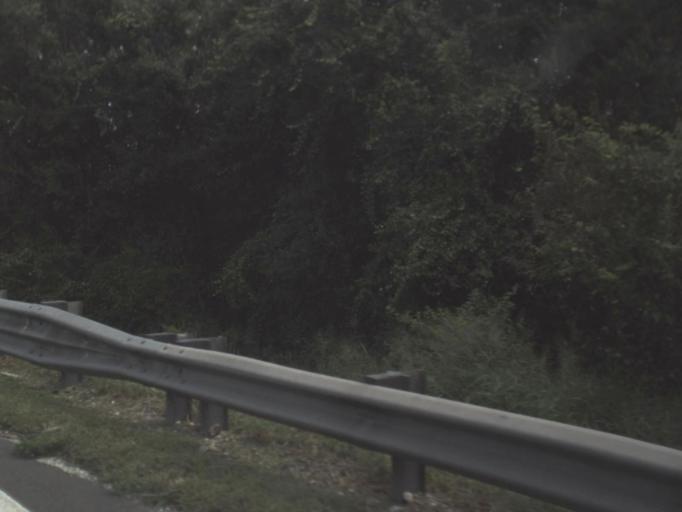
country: US
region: Florida
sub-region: Hardee County
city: Zolfo Springs
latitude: 27.3762
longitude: -81.7962
